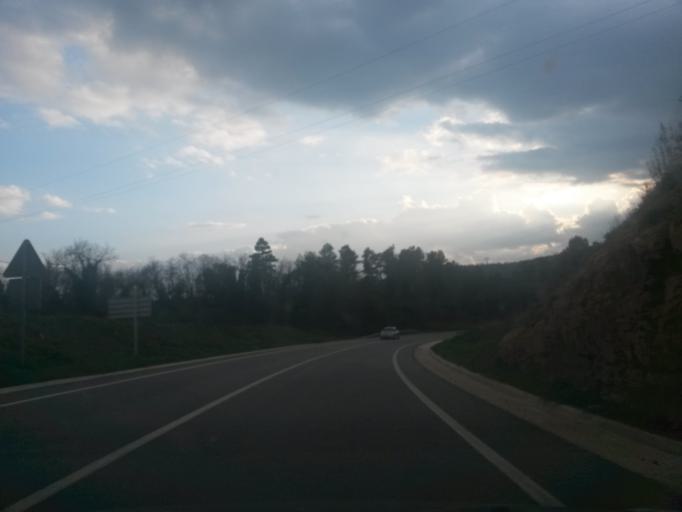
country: ES
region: Catalonia
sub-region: Provincia de Barcelona
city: Sagas
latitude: 42.0195
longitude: 1.9930
